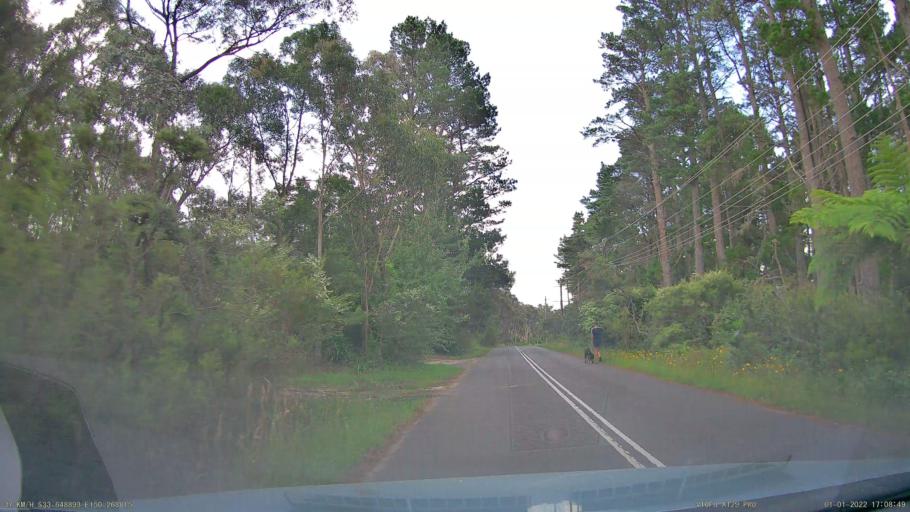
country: AU
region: New South Wales
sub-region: Blue Mountains Municipality
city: Blackheath
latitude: -33.6488
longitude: 150.2688
